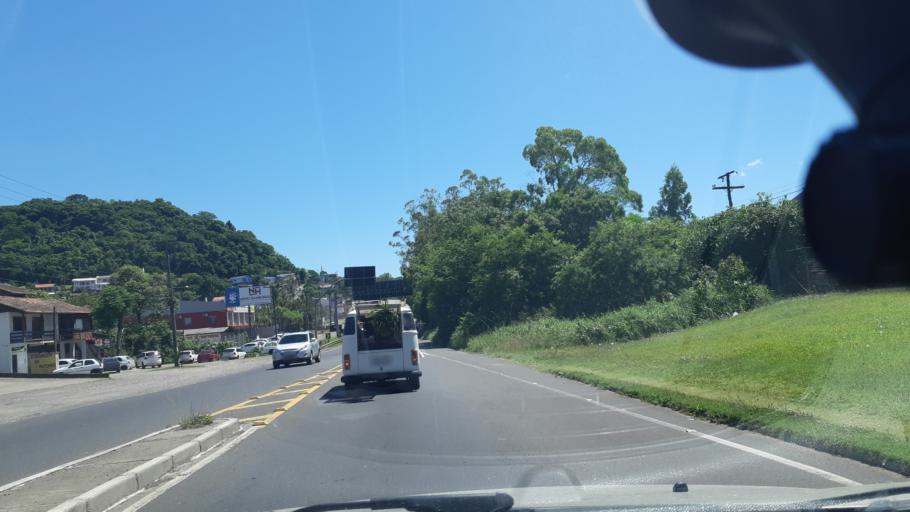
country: BR
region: Rio Grande do Sul
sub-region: Estancia Velha
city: Estancia Velha
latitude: -29.6484
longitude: -51.1439
